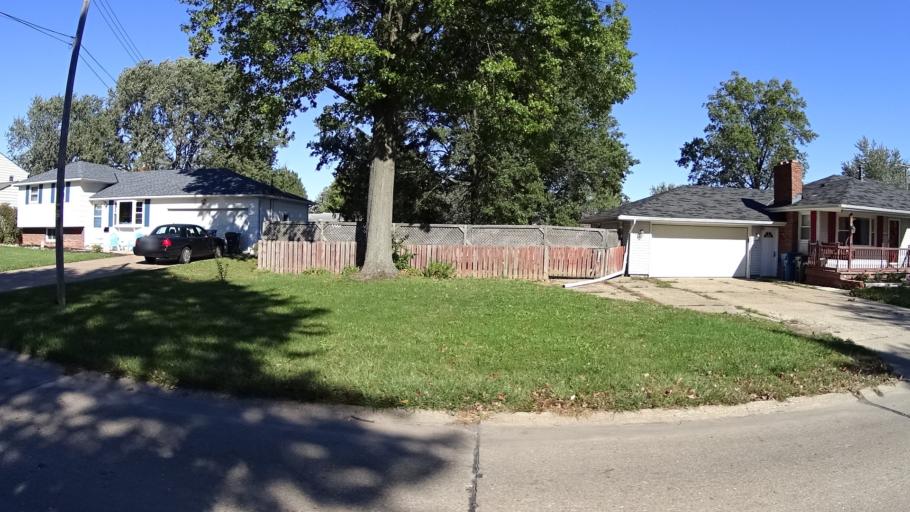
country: US
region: Ohio
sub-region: Lorain County
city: Amherst
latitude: 41.4023
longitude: -82.2399
